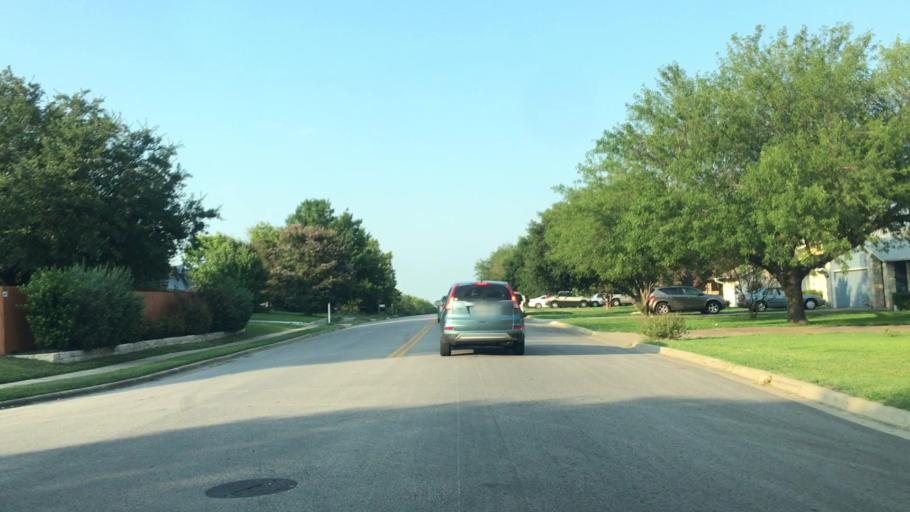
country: US
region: Texas
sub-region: Williamson County
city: Round Rock
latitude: 30.4983
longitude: -97.6647
